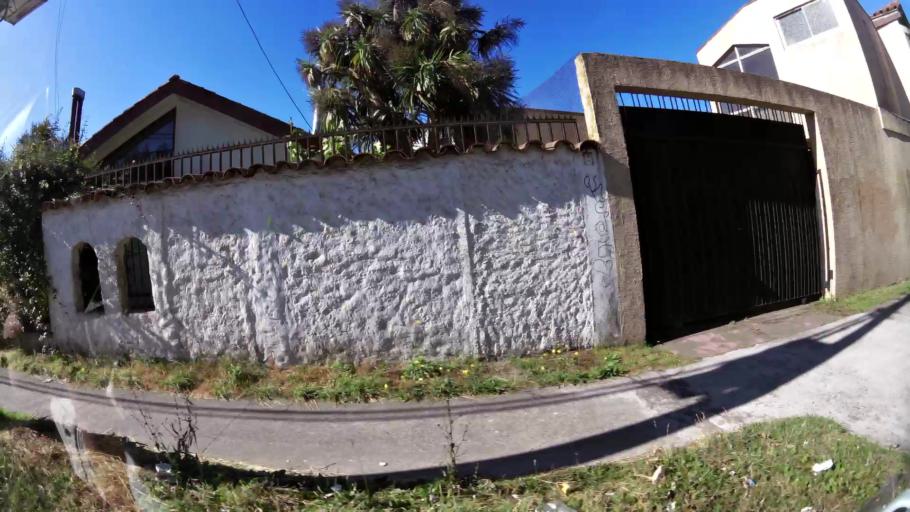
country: CL
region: Biobio
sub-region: Provincia de Concepcion
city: Concepcion
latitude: -36.8431
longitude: -73.1110
